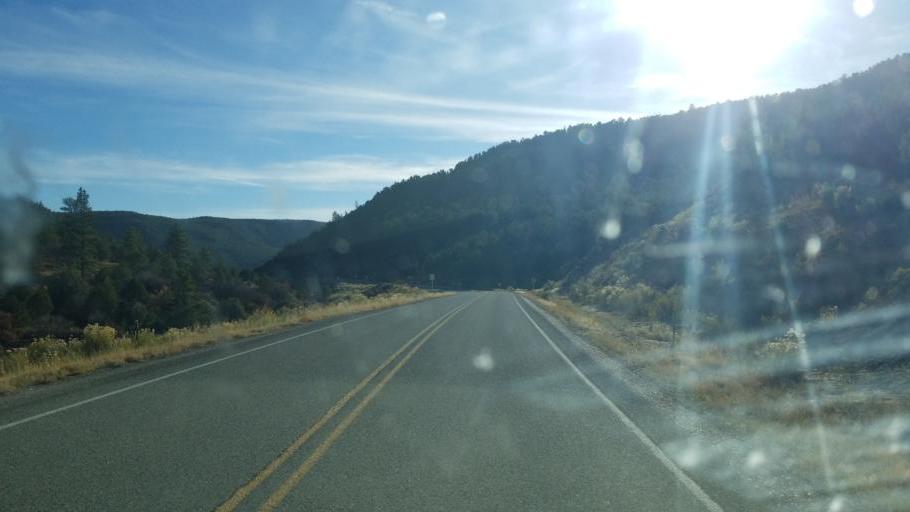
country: US
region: New Mexico
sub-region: Rio Arriba County
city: Navajo
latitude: 36.7304
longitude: -107.2778
